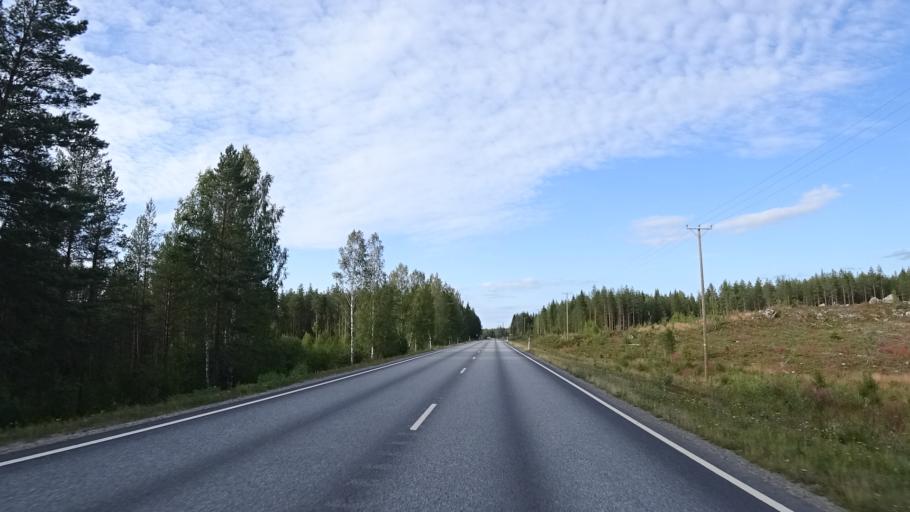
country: FI
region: North Karelia
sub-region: Joensuu
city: Eno
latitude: 62.8586
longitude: 30.1959
